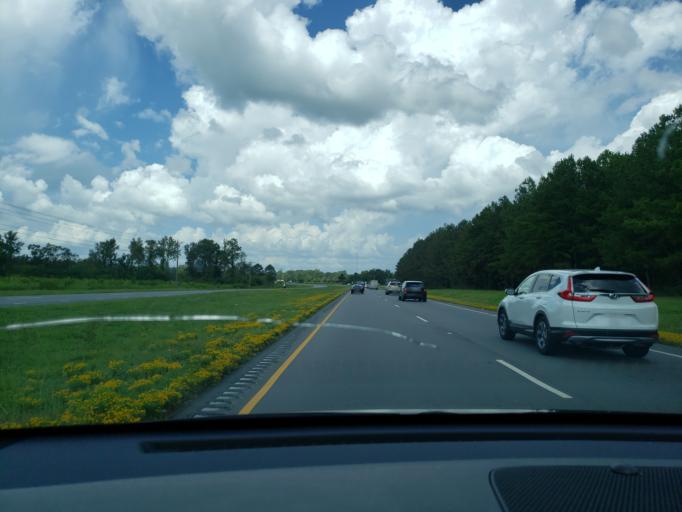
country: US
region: North Carolina
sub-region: Robeson County
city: Saint Pauls
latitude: 34.7789
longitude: -78.8105
